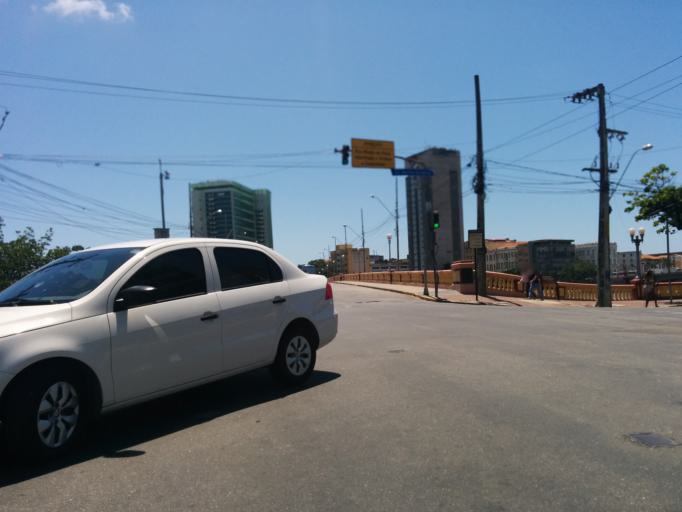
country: BR
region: Pernambuco
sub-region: Recife
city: Recife
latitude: -8.0616
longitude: -34.8767
